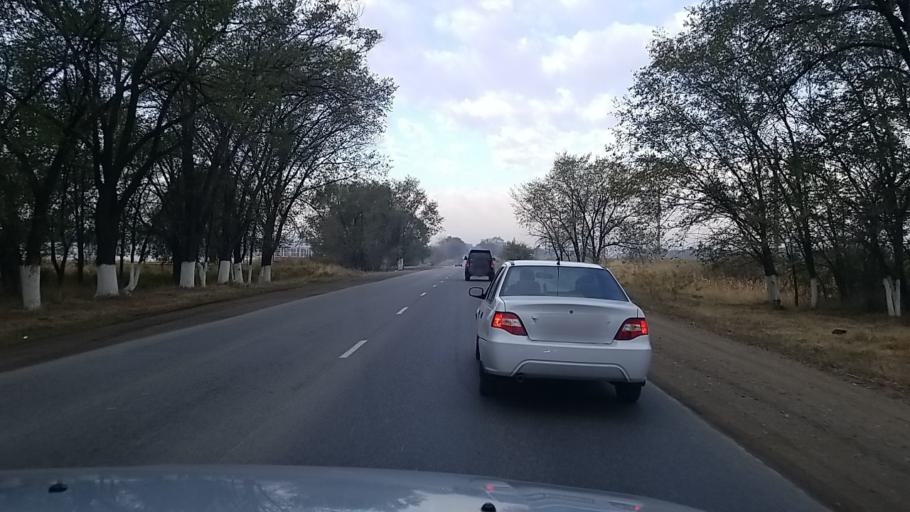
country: KZ
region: Almaty Oblysy
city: Burunday
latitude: 43.3584
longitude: 76.7740
